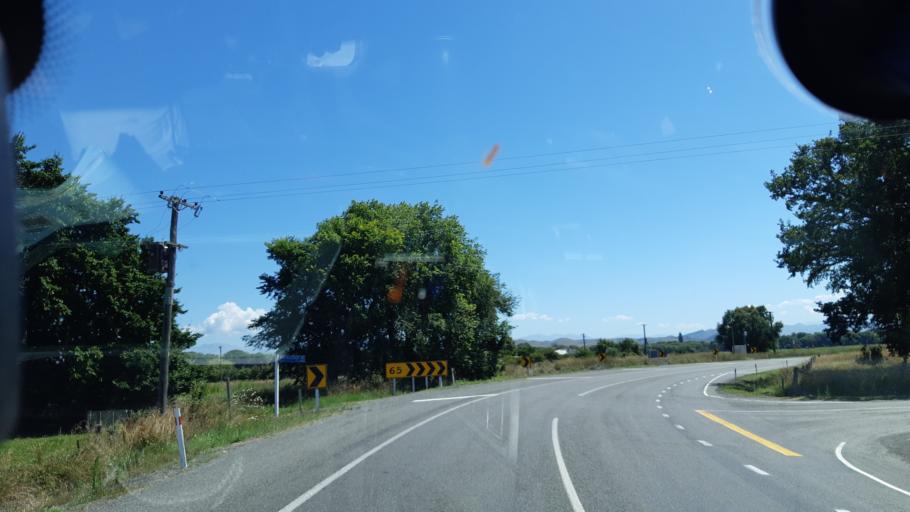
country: NZ
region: Canterbury
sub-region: Kaikoura District
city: Kaikoura
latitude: -42.7399
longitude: 173.2665
